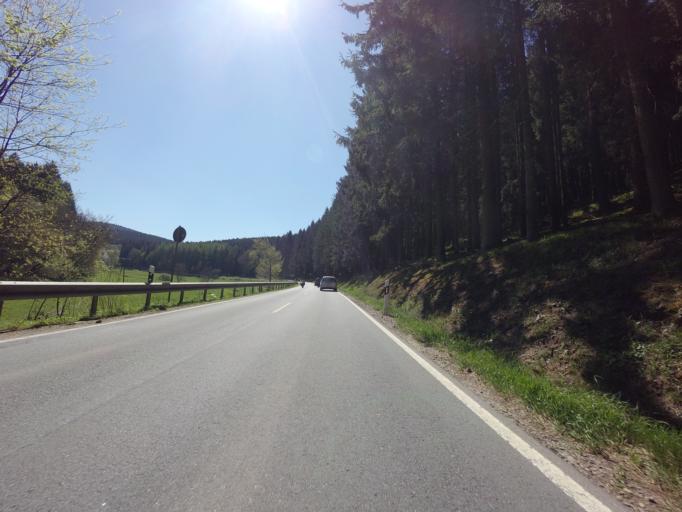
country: DE
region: North Rhine-Westphalia
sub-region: Regierungsbezirk Arnsberg
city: Kirchhundem
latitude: 51.0865
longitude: 8.1443
